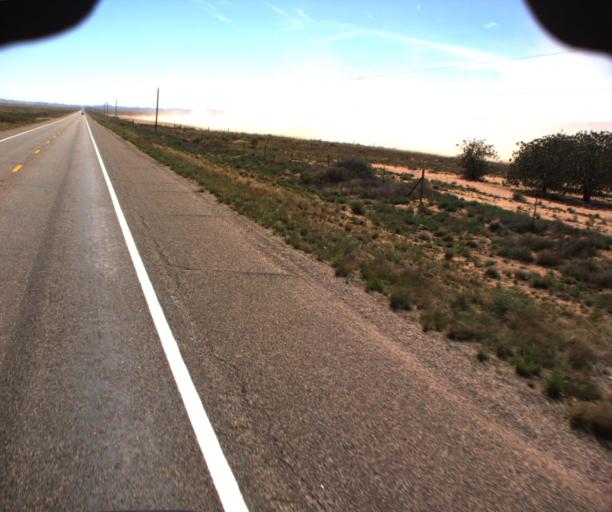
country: US
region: Arizona
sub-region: Mohave County
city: New Kingman-Butler
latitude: 35.3512
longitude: -113.8825
